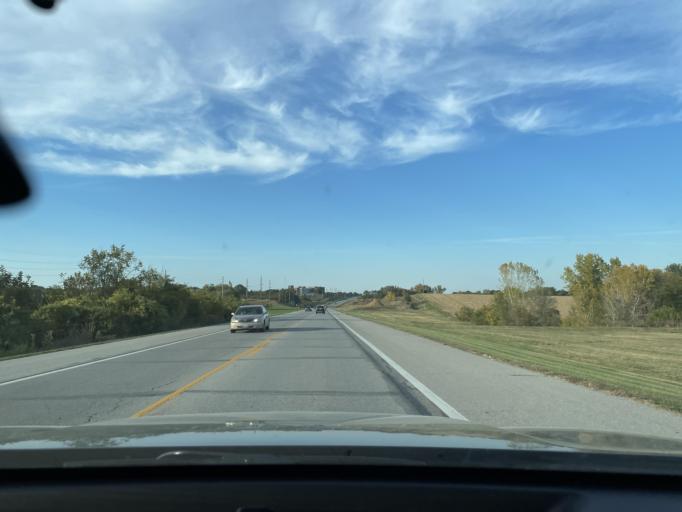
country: US
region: Missouri
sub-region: Buchanan County
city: Saint Joseph
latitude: 39.7596
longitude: -94.7684
